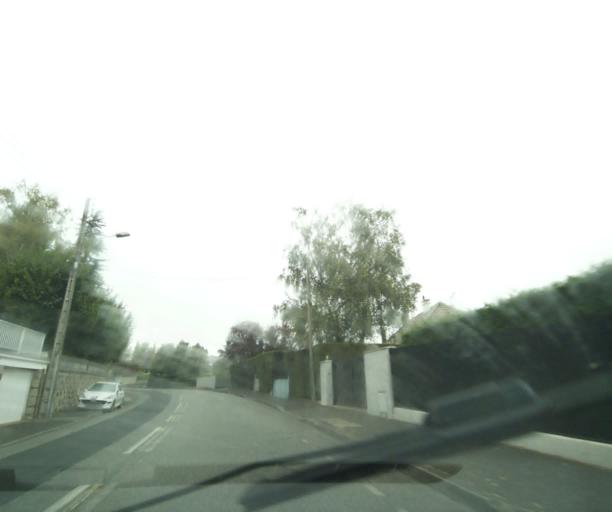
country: FR
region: Auvergne
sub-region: Departement du Puy-de-Dome
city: Chamalieres
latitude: 45.7852
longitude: 3.0571
